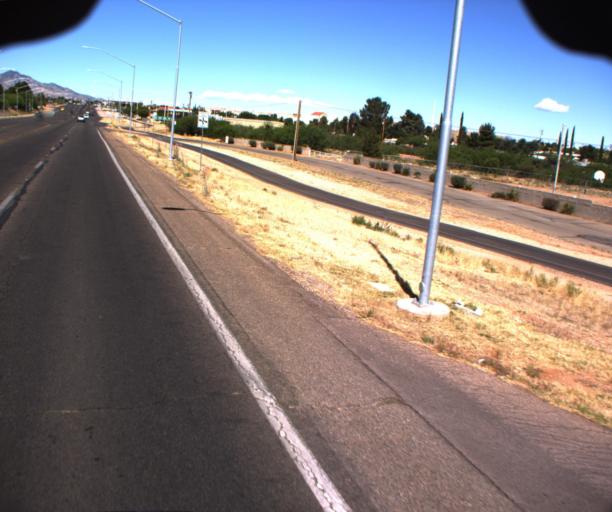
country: US
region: Arizona
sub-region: Cochise County
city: Sierra Vista
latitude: 31.5547
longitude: -110.2497
